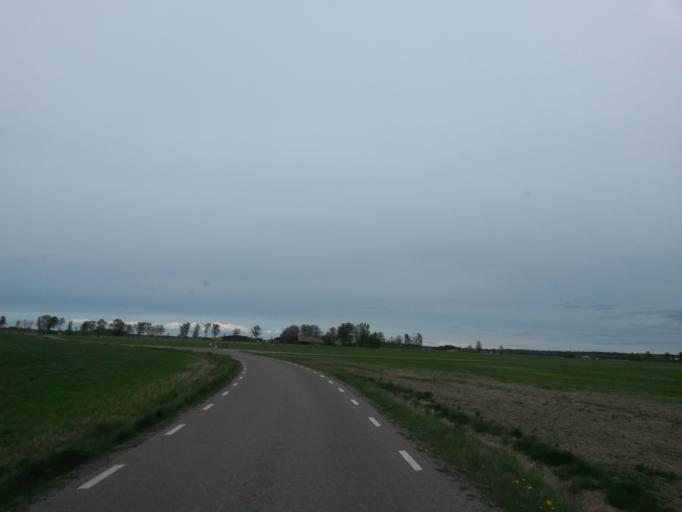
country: SE
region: Vaestra Goetaland
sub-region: Grastorps Kommun
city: Graestorp
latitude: 58.3579
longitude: 12.7830
